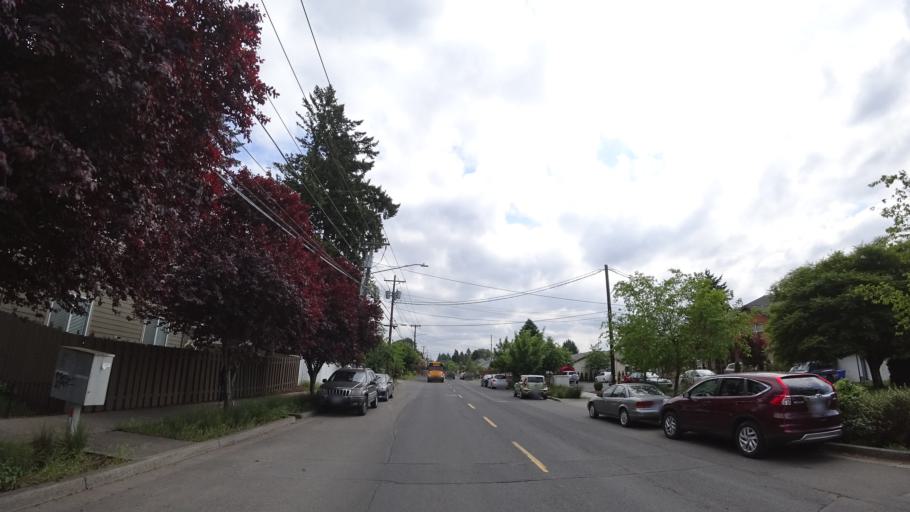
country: US
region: Oregon
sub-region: Multnomah County
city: Gresham
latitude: 45.5082
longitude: -122.4847
